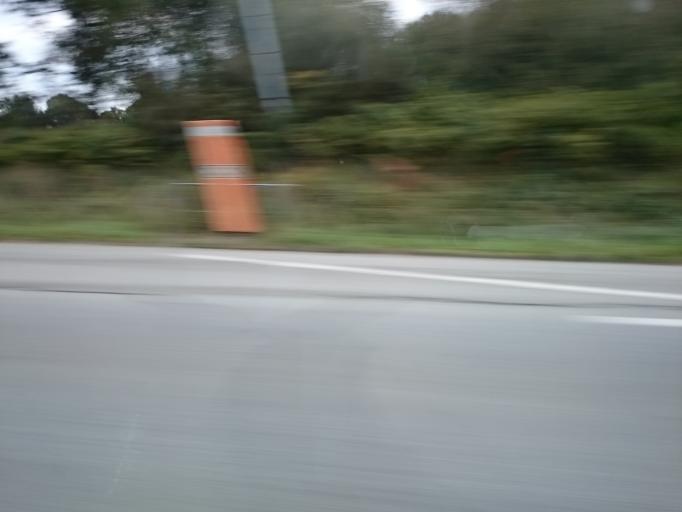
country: FR
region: Brittany
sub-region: Departement du Morbihan
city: Nostang
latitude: 47.7693
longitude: -3.1698
